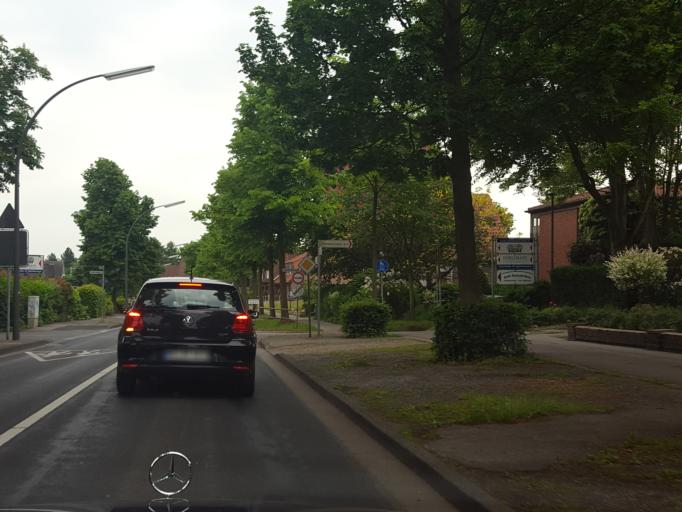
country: DE
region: North Rhine-Westphalia
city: Oer-Erkenschwick
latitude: 51.6243
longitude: 7.2507
